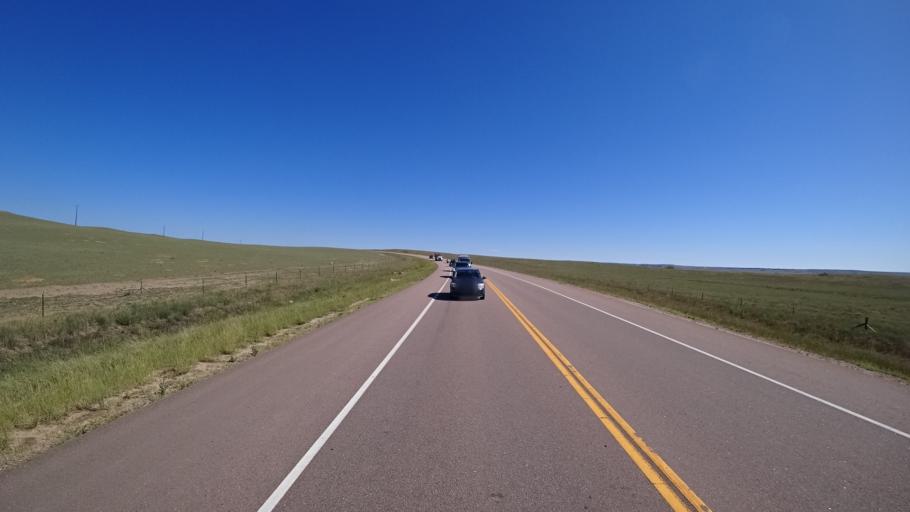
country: US
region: Colorado
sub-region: El Paso County
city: Security-Widefield
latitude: 38.7901
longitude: -104.6576
